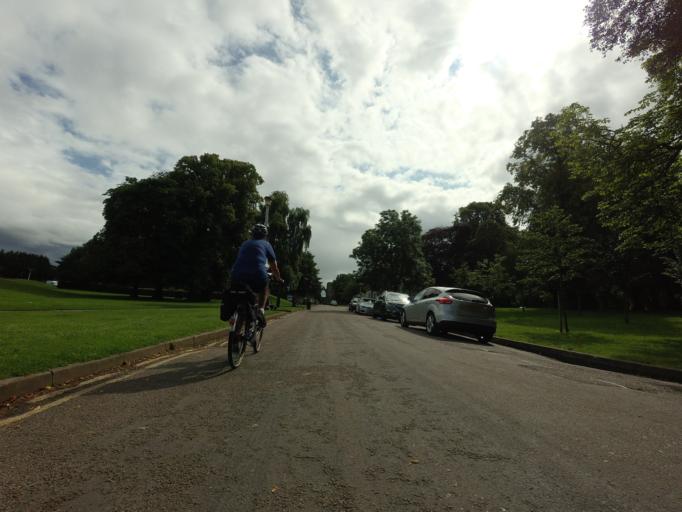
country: GB
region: Scotland
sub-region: Moray
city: Elgin
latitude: 57.6507
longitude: -3.3114
